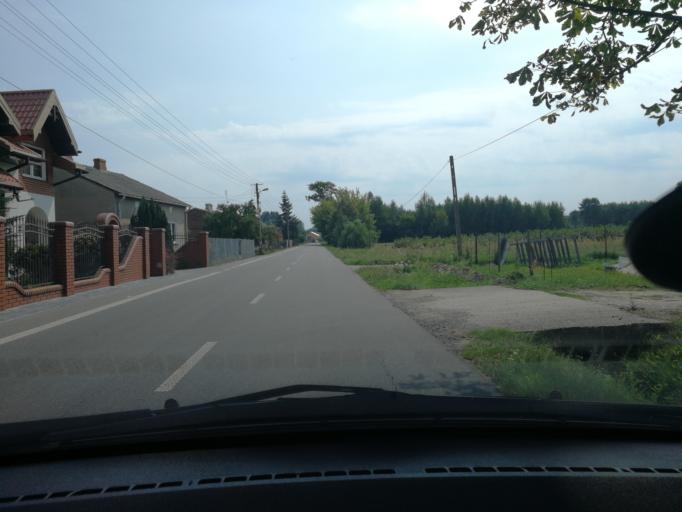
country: PL
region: Lodz Voivodeship
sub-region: powiat Lowicki
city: Nieborow
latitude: 52.0147
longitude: 20.0618
